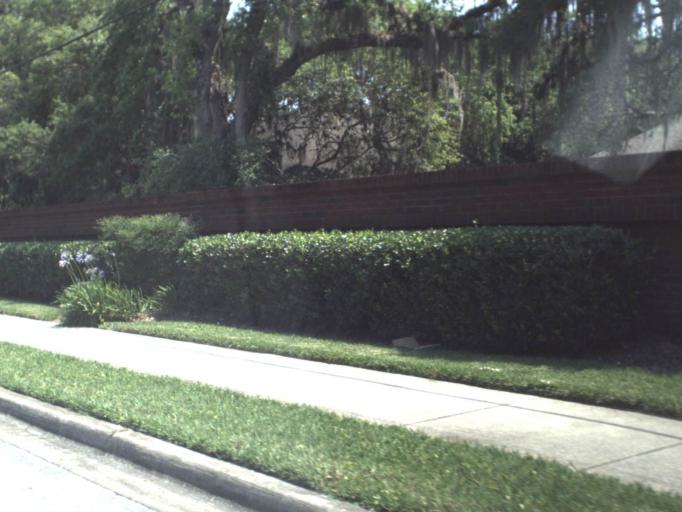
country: US
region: Florida
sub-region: Saint Johns County
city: Saint Augustine Beach
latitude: 29.8350
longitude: -81.2745
